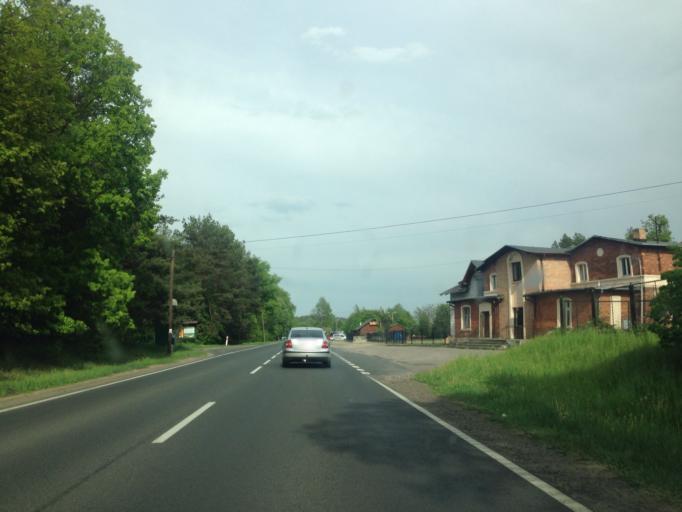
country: PL
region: Kujawsko-Pomorskie
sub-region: Powiat brodnicki
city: Brodnica
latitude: 53.2803
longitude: 19.4656
